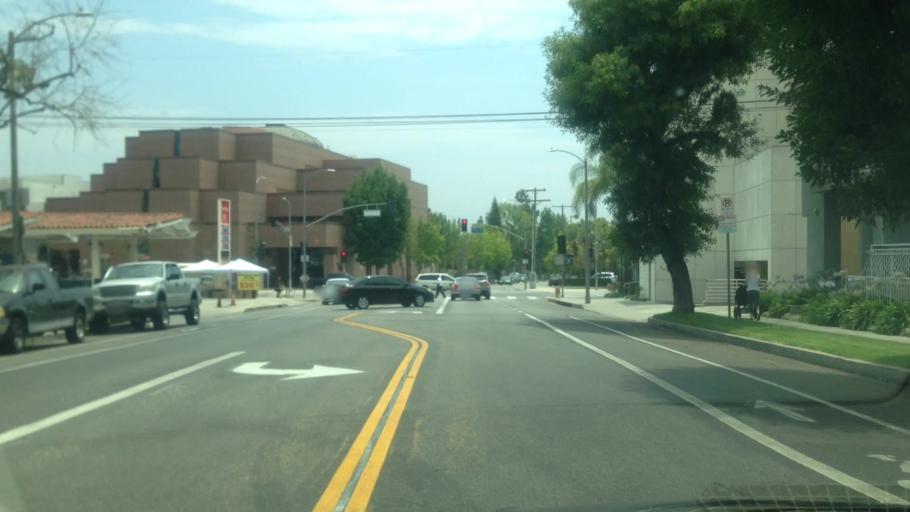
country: US
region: California
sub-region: Los Angeles County
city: Century City
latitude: 34.0547
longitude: -118.4026
